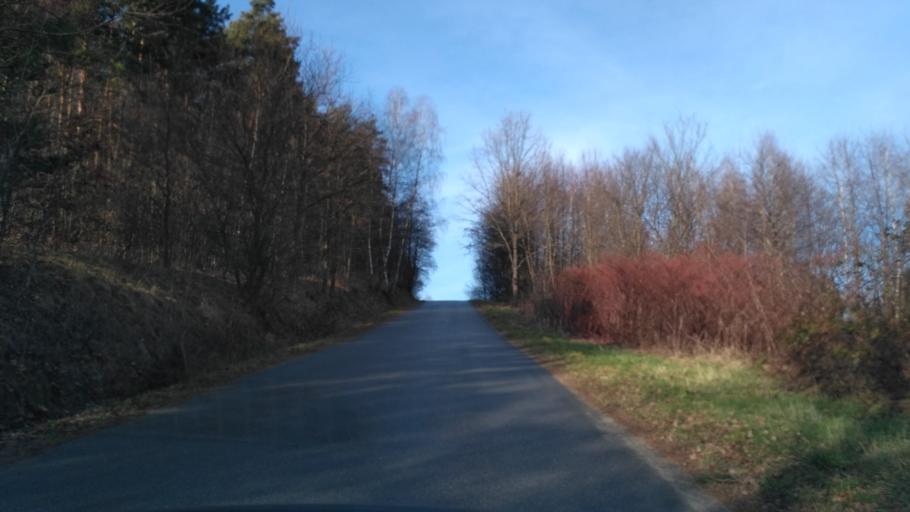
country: PL
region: Subcarpathian Voivodeship
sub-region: Powiat krosnienski
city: Korczyna
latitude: 49.7290
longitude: 21.7912
